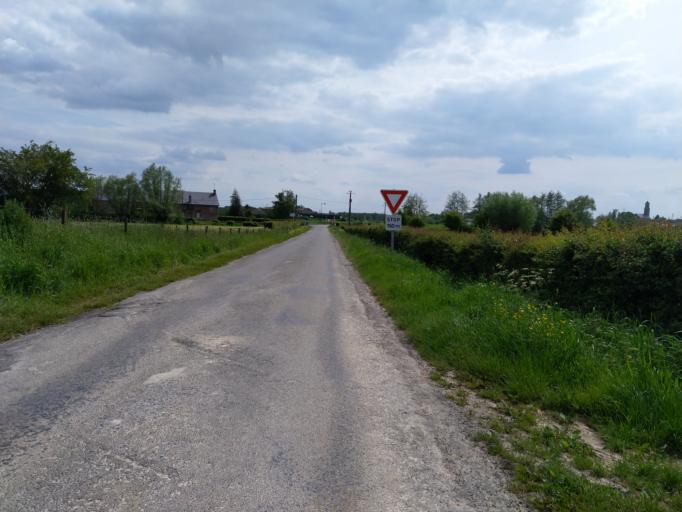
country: FR
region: Picardie
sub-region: Departement de l'Aisne
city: Boue
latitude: 50.0273
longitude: 3.6785
